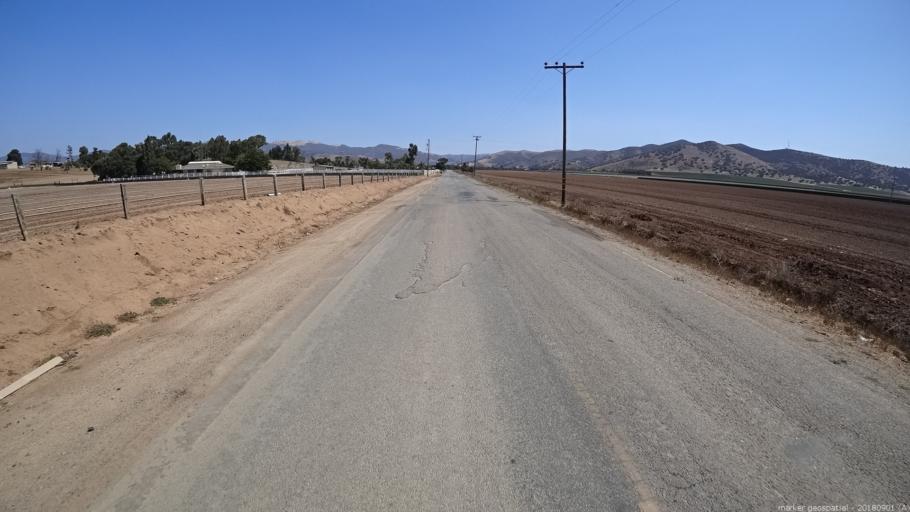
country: US
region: California
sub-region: Monterey County
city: Chualar
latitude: 36.5869
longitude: -121.4666
